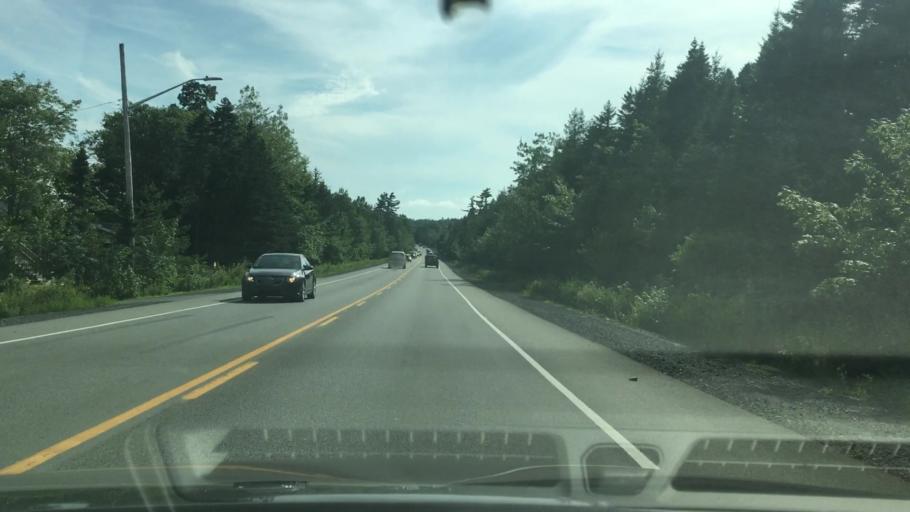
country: CA
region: Nova Scotia
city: Dartmouth
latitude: 44.7317
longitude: -63.8100
